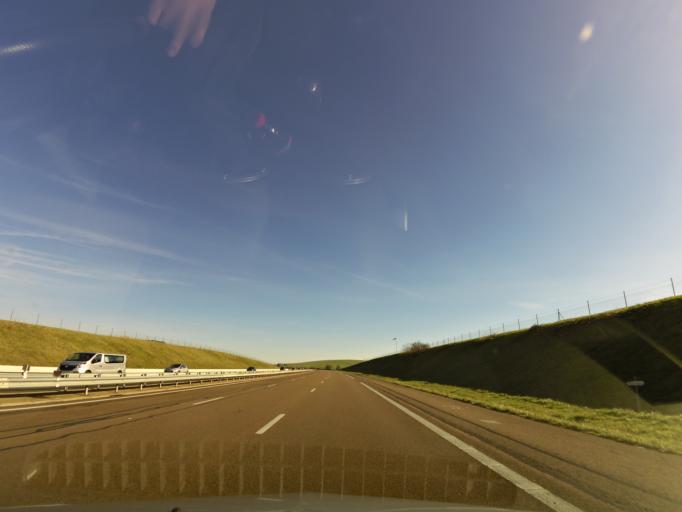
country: FR
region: Bourgogne
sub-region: Departement de l'Yonne
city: Aillant-sur-Tholon
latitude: 47.8989
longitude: 3.3606
